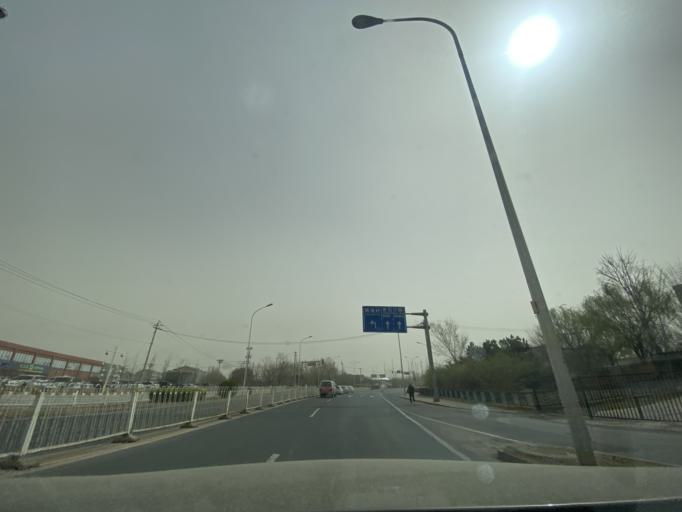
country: CN
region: Beijing
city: Sijiqing
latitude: 39.9536
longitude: 116.2300
